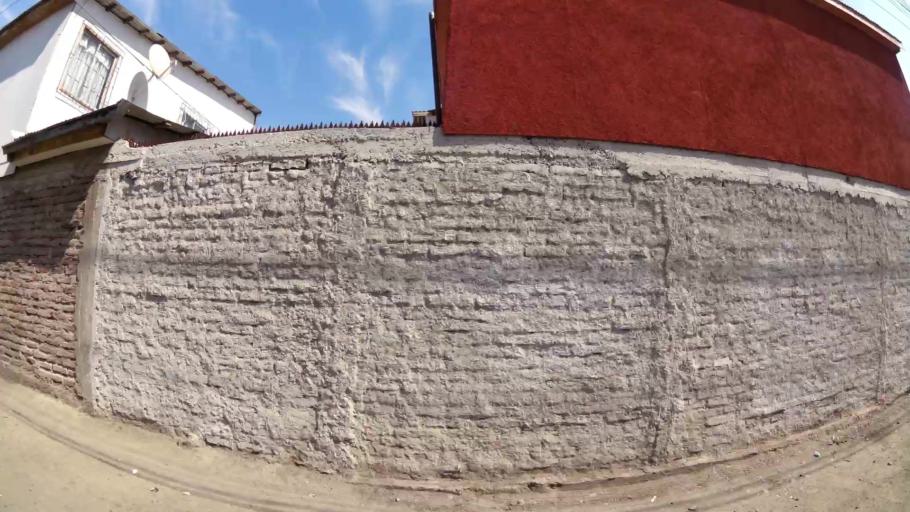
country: CL
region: Santiago Metropolitan
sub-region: Provincia de Santiago
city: La Pintana
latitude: -33.5577
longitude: -70.6398
